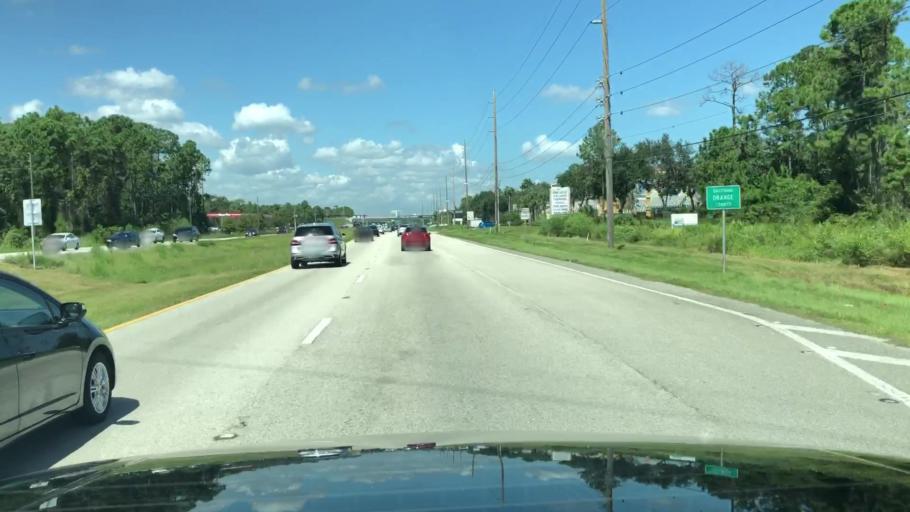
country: US
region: Florida
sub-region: Osceola County
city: Celebration
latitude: 28.3472
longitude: -81.4876
